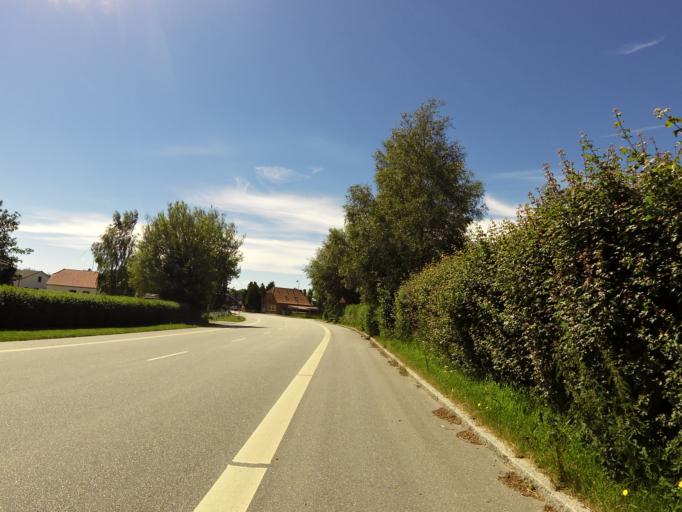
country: DK
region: South Denmark
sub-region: Aabenraa Kommune
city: Rodekro
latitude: 55.0253
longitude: 9.3145
